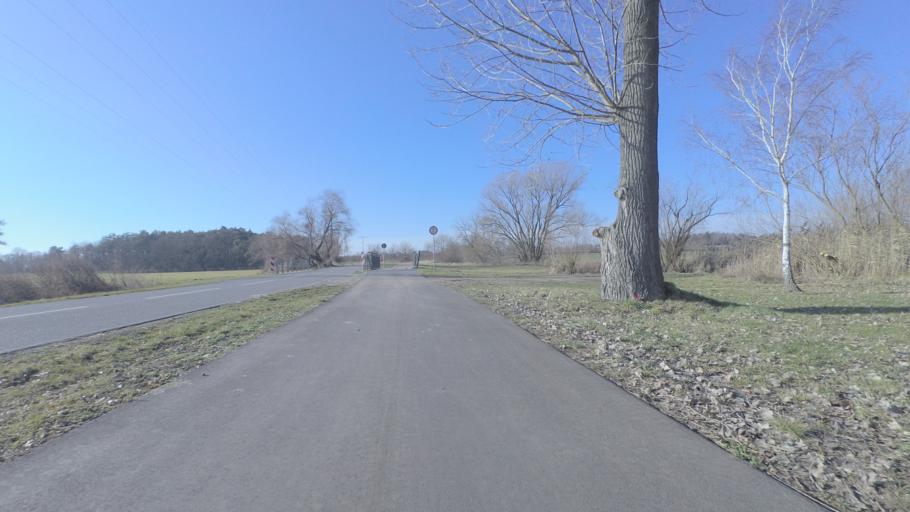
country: DE
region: Brandenburg
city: Juterbog
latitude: 52.0090
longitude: 13.1138
